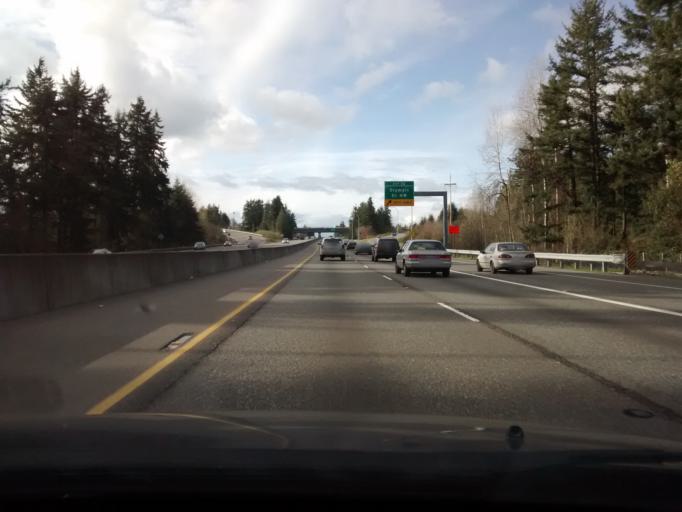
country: US
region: Washington
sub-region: Pierce County
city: Gig Harbor
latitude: 47.3013
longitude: -122.5728
